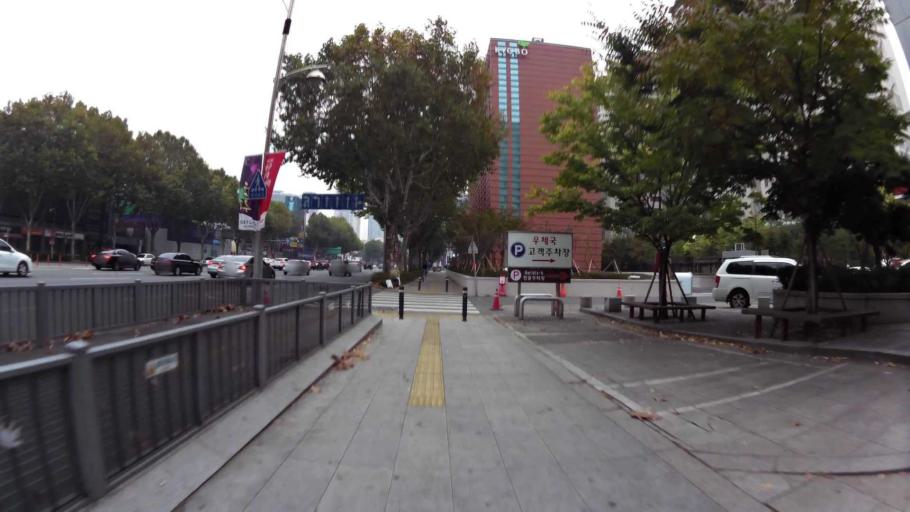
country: KR
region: Daegu
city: Daegu
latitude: 35.8595
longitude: 128.6161
